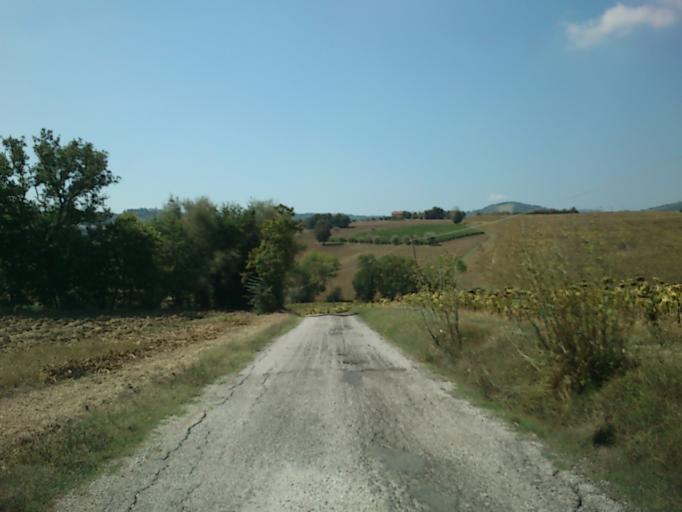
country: IT
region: The Marches
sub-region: Provincia di Pesaro e Urbino
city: Lucrezia
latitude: 43.7841
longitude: 12.9196
